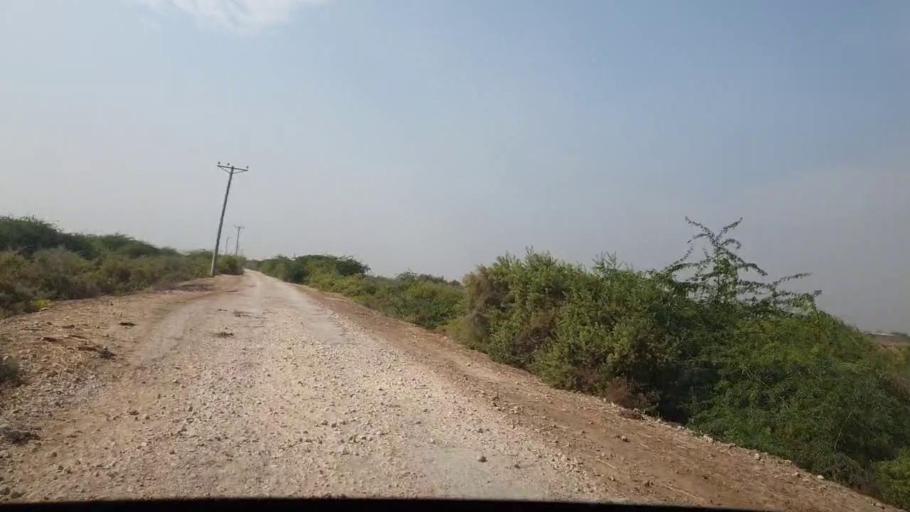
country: PK
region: Sindh
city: Chuhar Jamali
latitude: 24.2724
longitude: 67.9022
